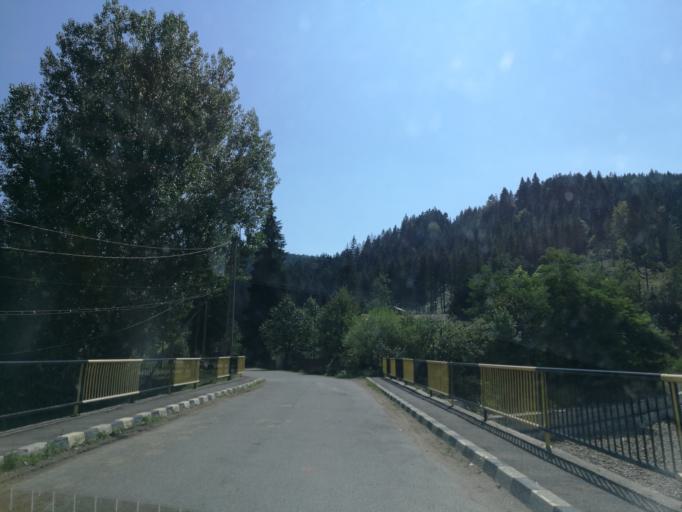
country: RO
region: Suceava
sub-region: Comuna Putna
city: Putna
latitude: 47.8669
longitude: 25.6132
